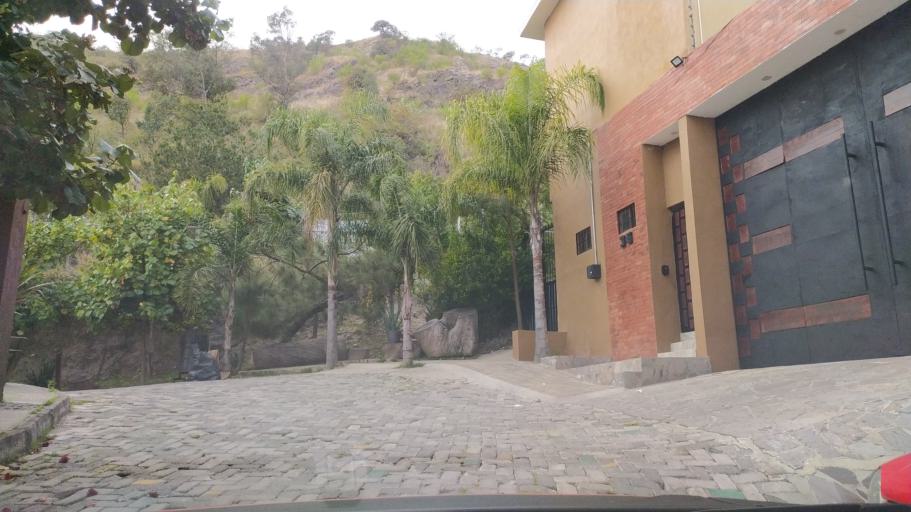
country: MX
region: Jalisco
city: Guadalajara
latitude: 20.6612
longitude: -103.4562
